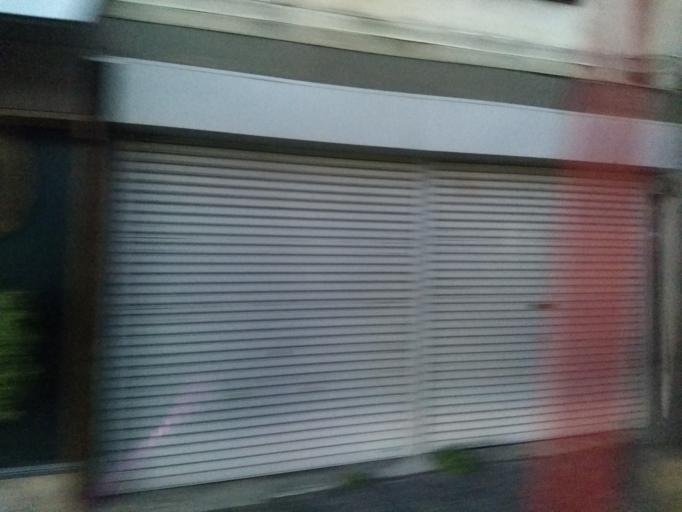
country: JP
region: Chiba
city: Kashiwa
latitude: 35.8652
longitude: 139.9657
